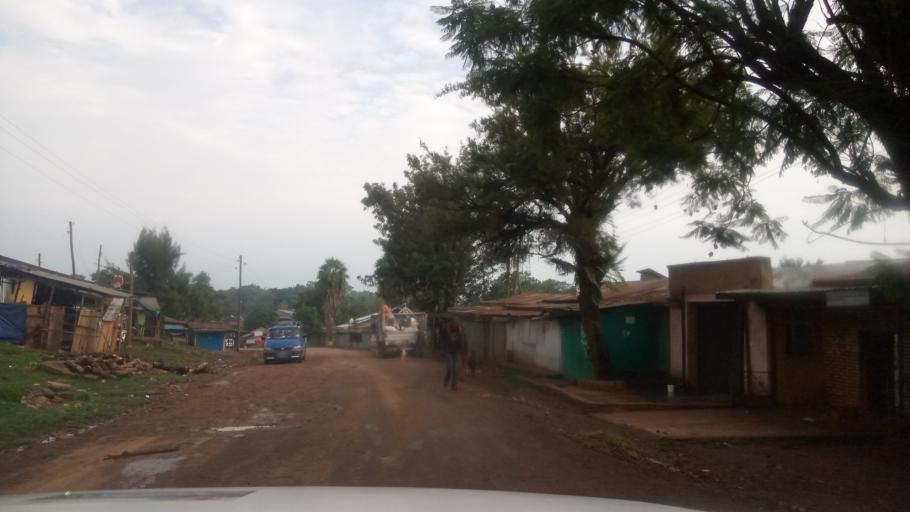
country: ET
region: Oromiya
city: Agaro
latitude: 7.8371
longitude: 36.6710
